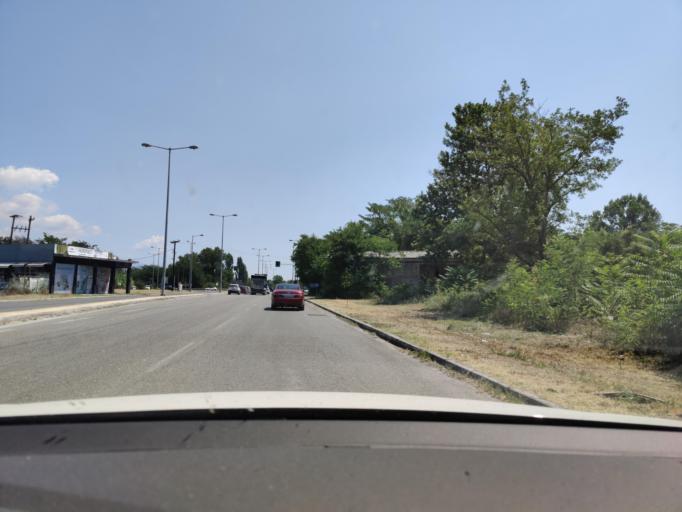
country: GR
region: Central Macedonia
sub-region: Nomos Serron
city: Serres
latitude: 41.0758
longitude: 23.5387
